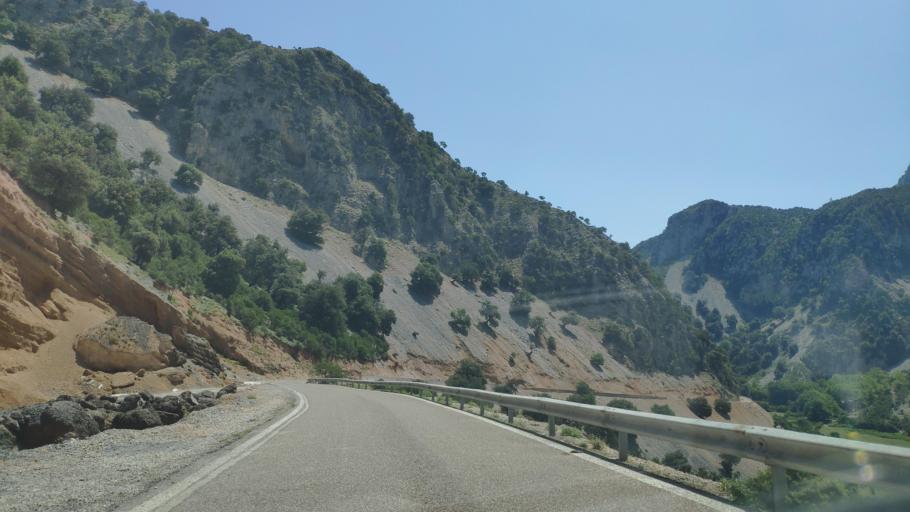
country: GR
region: West Greece
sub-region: Nomos Aitolias kai Akarnanias
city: Krikellos
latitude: 39.0089
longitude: 21.3637
